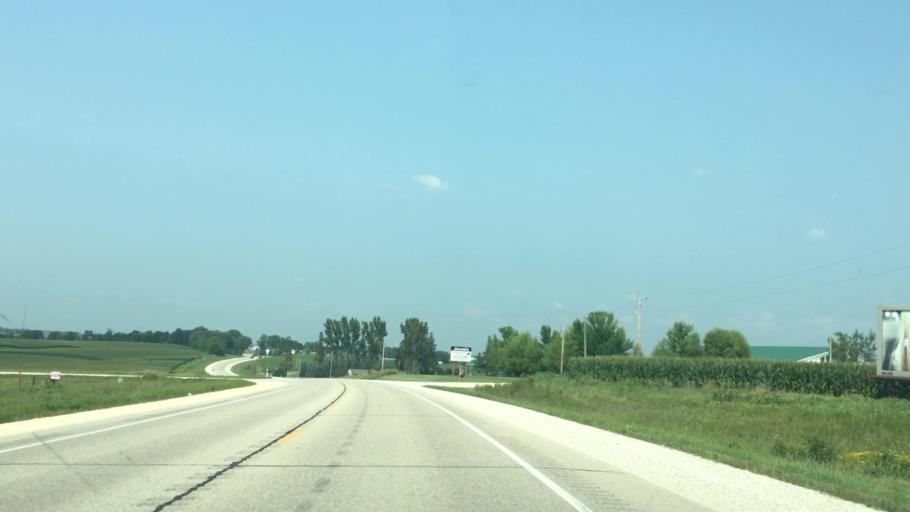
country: US
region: Iowa
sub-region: Winneshiek County
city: Decorah
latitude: 43.2544
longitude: -91.8387
